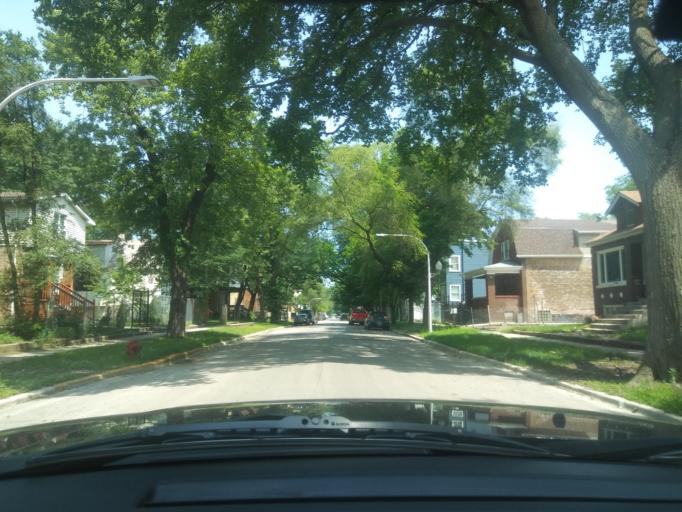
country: US
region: Illinois
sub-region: Cook County
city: Evergreen Park
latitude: 41.7801
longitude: -87.6715
